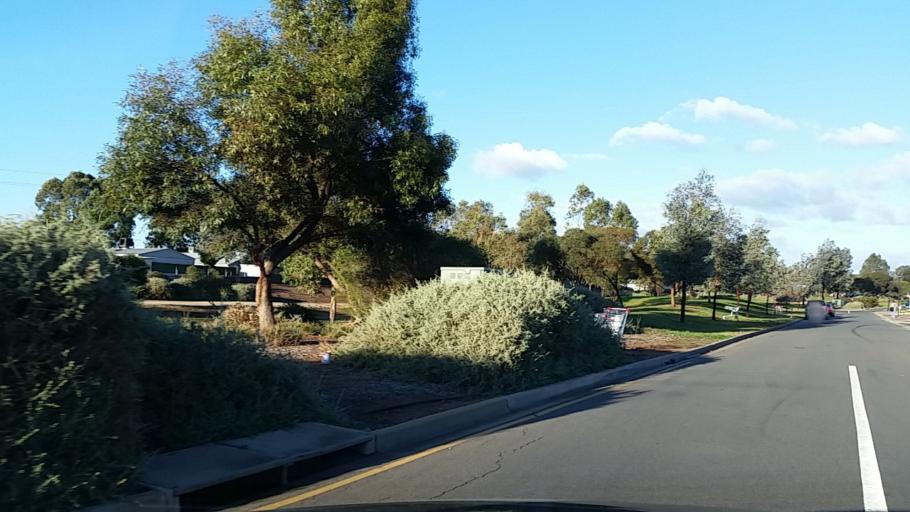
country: AU
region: South Australia
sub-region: Playford
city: Smithfield
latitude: -34.6806
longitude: 138.6830
